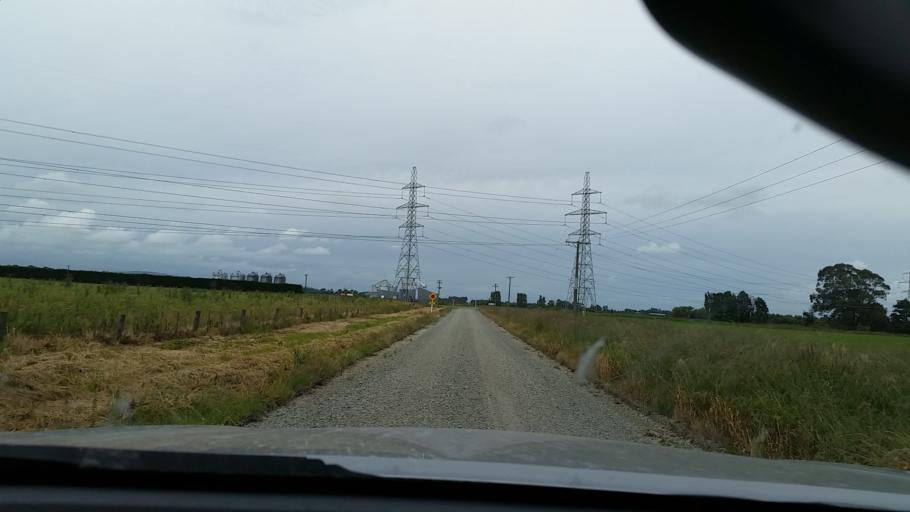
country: NZ
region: Southland
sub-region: Southland District
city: Winton
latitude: -46.2521
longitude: 168.2762
